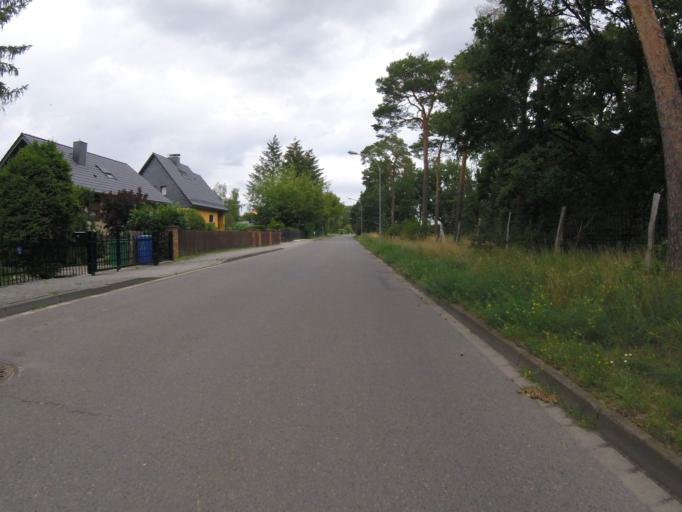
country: DE
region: Brandenburg
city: Konigs Wusterhausen
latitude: 52.2997
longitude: 13.6381
